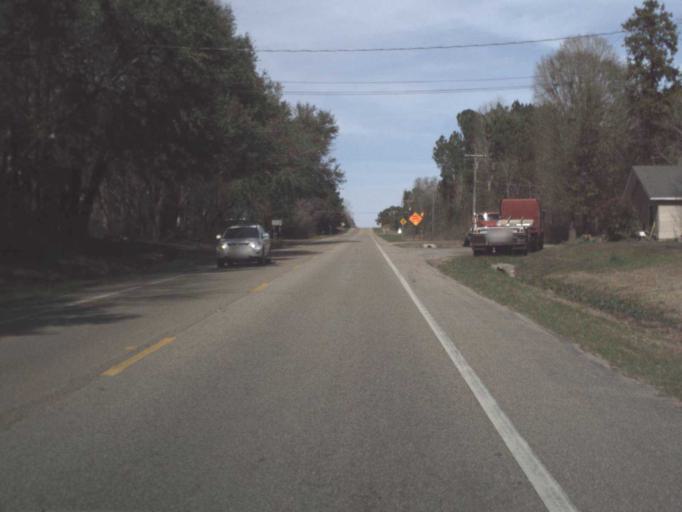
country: US
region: Florida
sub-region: Washington County
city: Chipley
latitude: 30.8601
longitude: -85.5278
